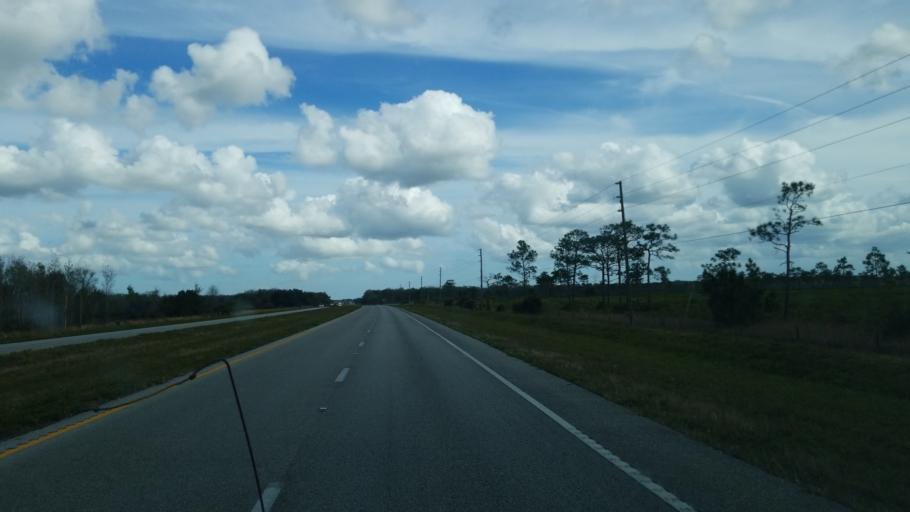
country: US
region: Florida
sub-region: Osceola County
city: Saint Cloud
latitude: 28.1321
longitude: -81.0143
